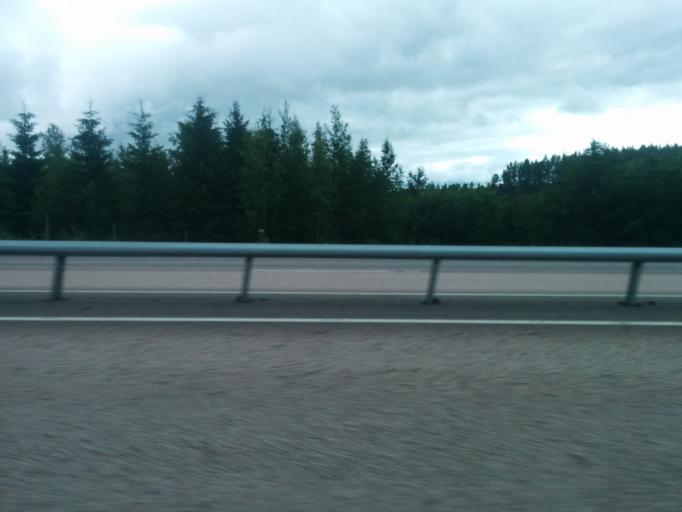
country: FI
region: Pirkanmaa
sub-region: Tampere
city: Orivesi
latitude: 61.7080
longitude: 24.5396
